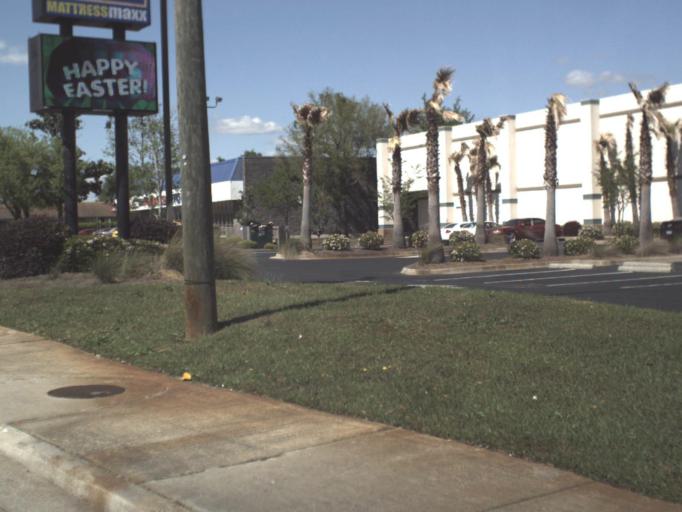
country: US
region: Florida
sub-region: Escambia County
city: Ferry Pass
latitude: 30.4894
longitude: -87.2233
